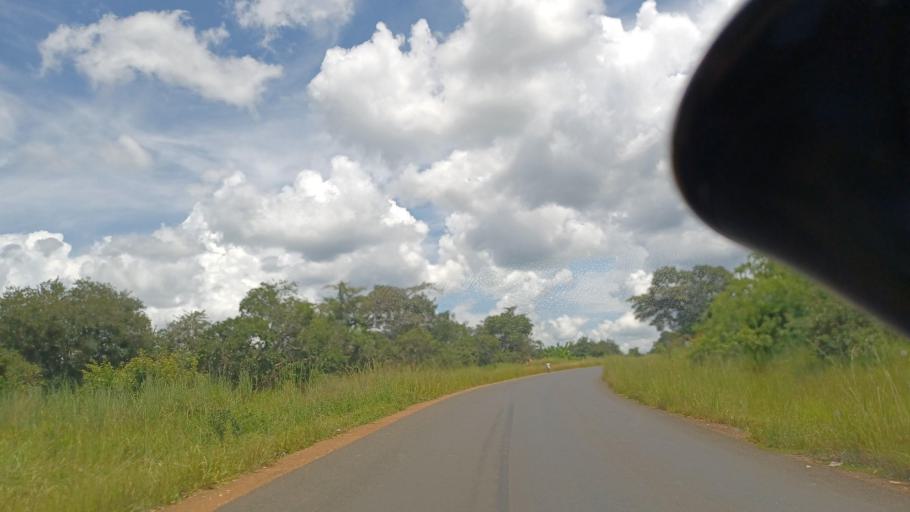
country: ZM
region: North-Western
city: Solwezi
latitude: -12.4063
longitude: 26.2399
